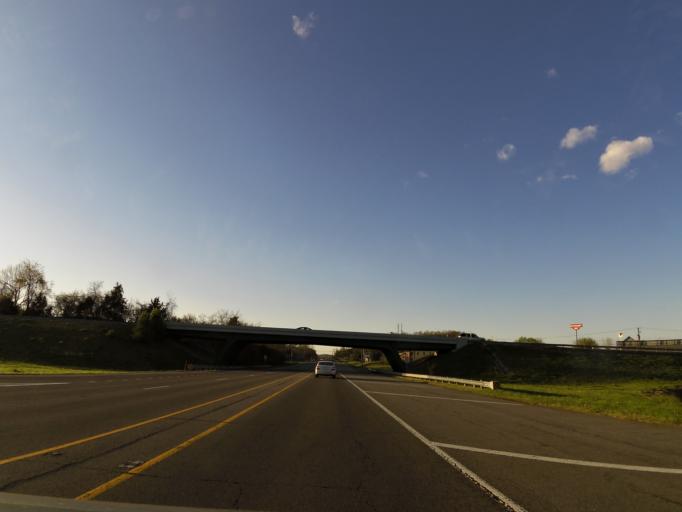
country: US
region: Tennessee
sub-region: Davidson County
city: Goodlettsville
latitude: 36.3423
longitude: -86.7191
